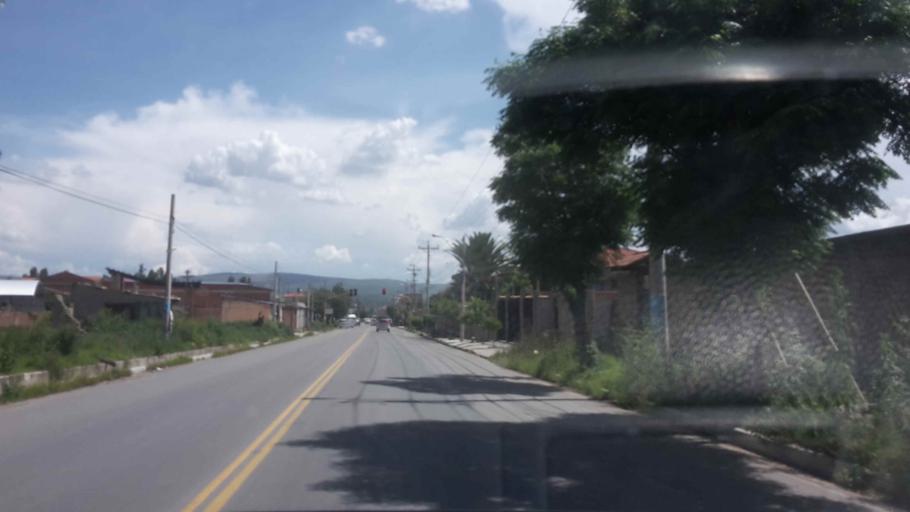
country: BO
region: Cochabamba
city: Cochabamba
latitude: -17.3806
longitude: -66.2354
